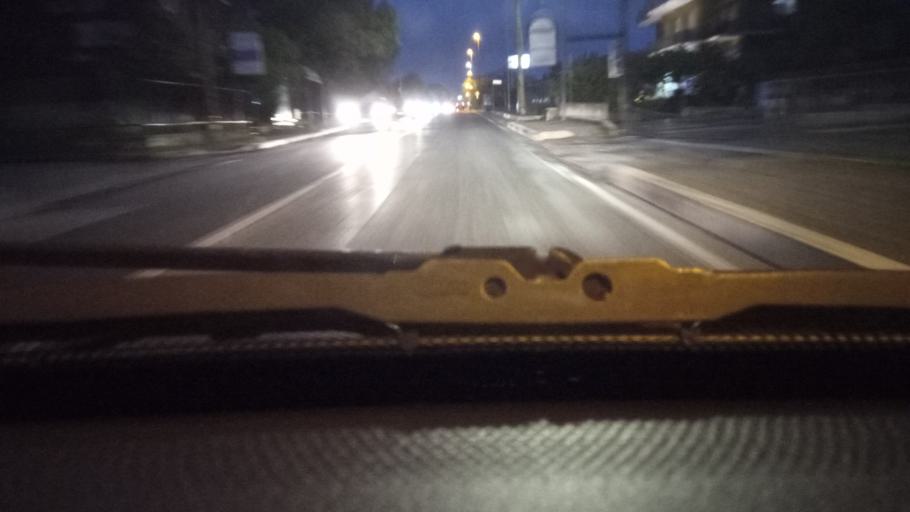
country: IT
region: Latium
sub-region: Provincia di Latina
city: Formia
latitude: 41.2621
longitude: 13.6498
